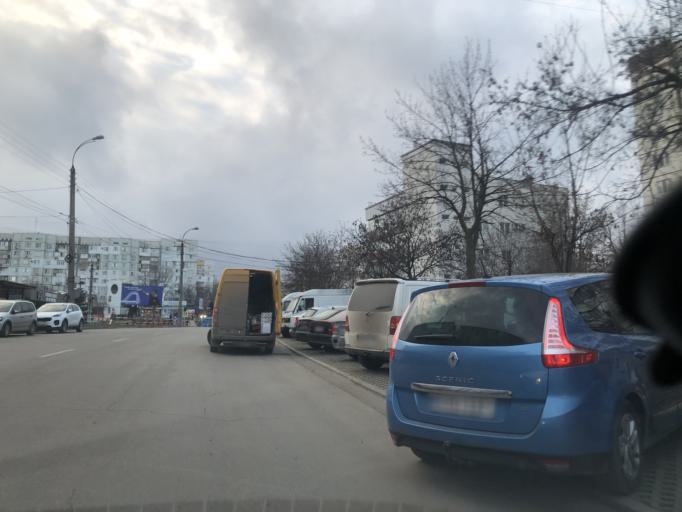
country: MD
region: Chisinau
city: Chisinau
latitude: 47.0430
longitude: 28.8921
